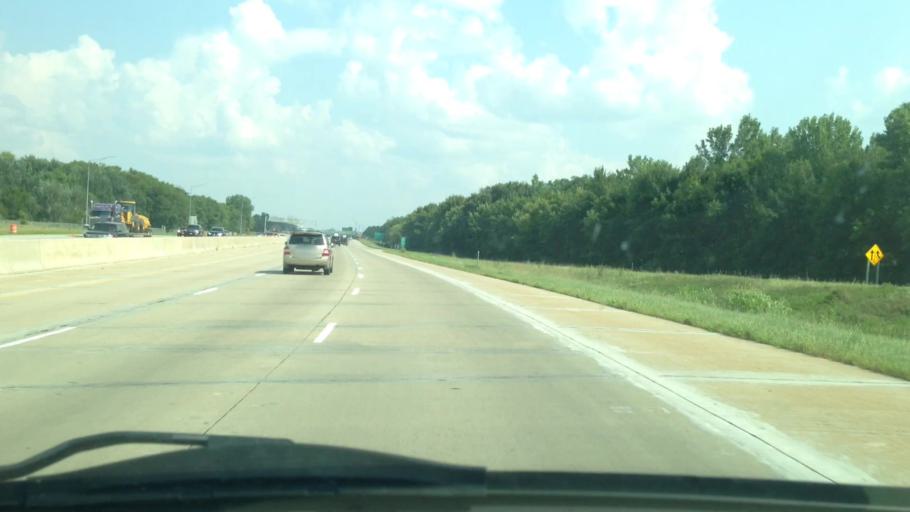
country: US
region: Iowa
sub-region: Black Hawk County
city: Waterloo
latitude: 42.5152
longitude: -92.3881
